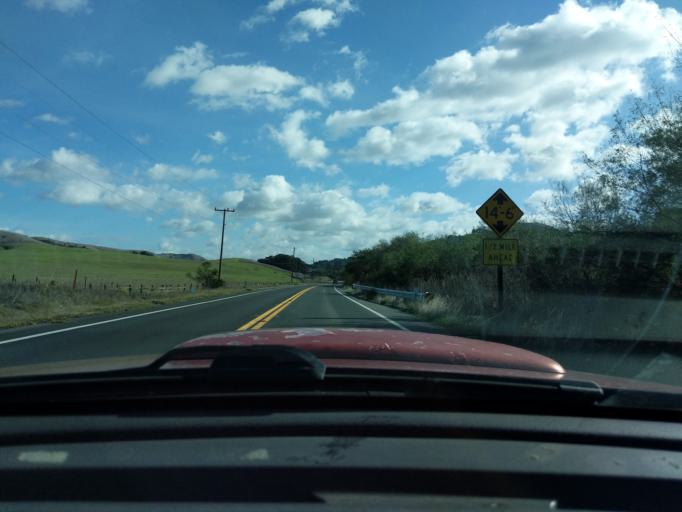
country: US
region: California
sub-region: San Benito County
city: Aromas
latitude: 36.9035
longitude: -121.6072
